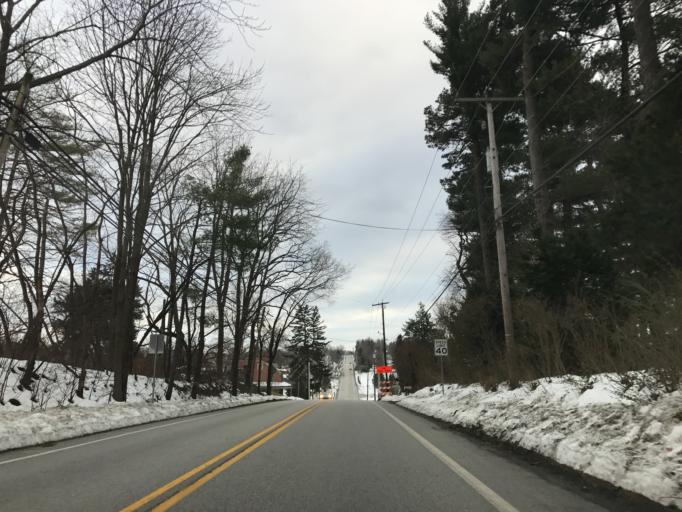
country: US
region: Pennsylvania
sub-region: York County
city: Grantley
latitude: 39.9188
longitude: -76.7150
